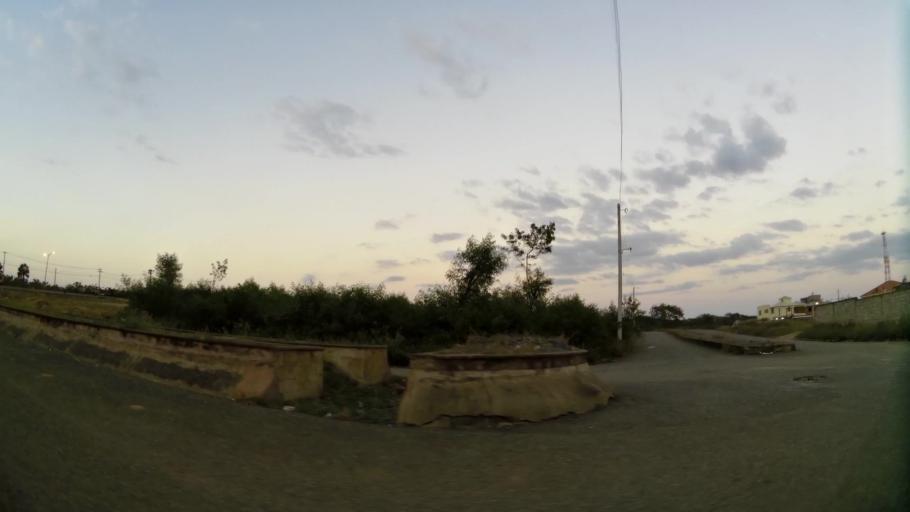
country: DO
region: Nacional
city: La Agustina
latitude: 18.5480
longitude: -69.9494
